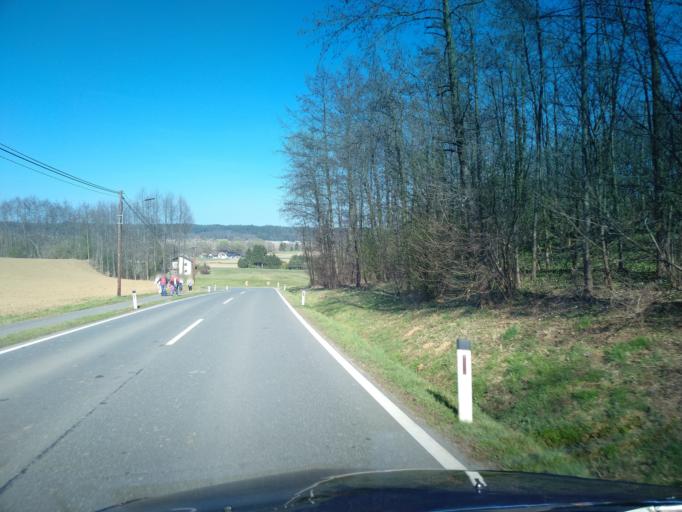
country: AT
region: Styria
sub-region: Politischer Bezirk Deutschlandsberg
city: Preding
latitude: 46.8954
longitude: 15.4056
